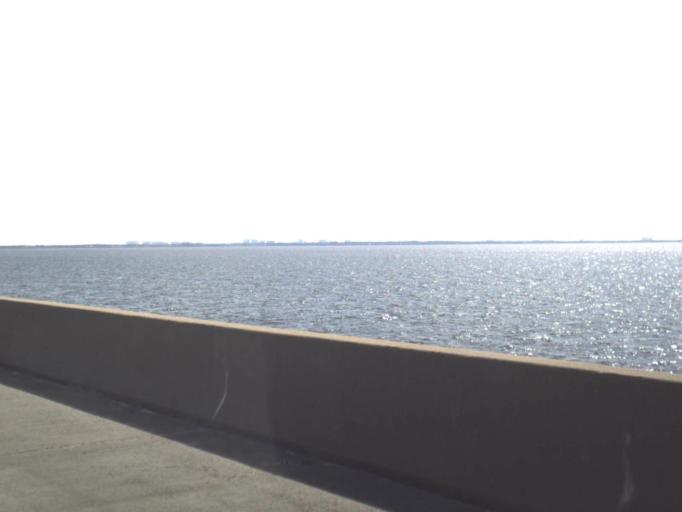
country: US
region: Florida
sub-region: Okaloosa County
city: Niceville
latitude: 30.4509
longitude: -86.4159
